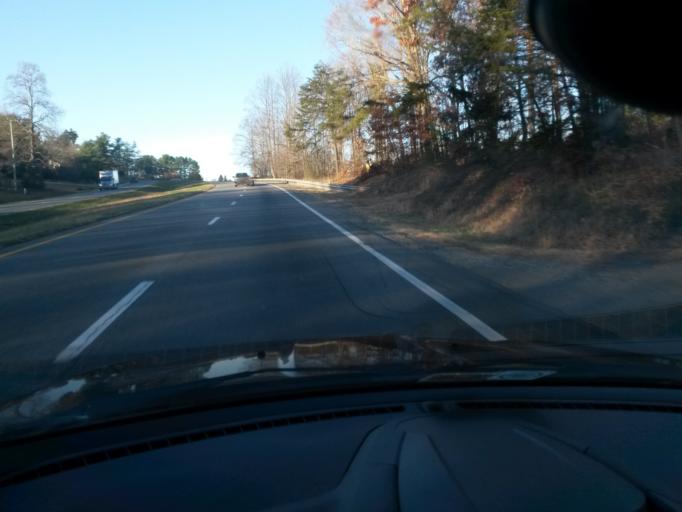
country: US
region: Virginia
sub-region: Henry County
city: Stanleytown
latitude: 36.8441
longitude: -79.9053
